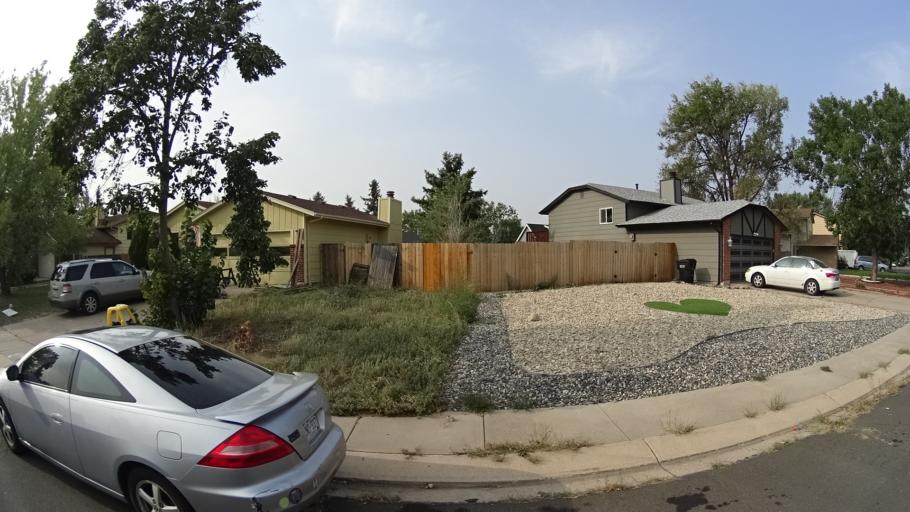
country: US
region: Colorado
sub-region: El Paso County
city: Stratmoor
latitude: 38.8003
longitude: -104.7417
